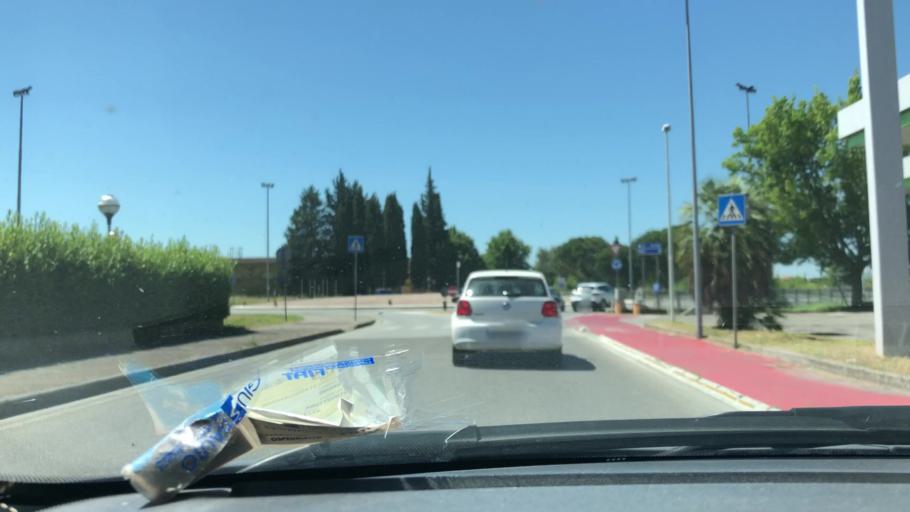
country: IT
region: Tuscany
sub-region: Province of Pisa
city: Pontedera
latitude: 43.6549
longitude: 10.6314
